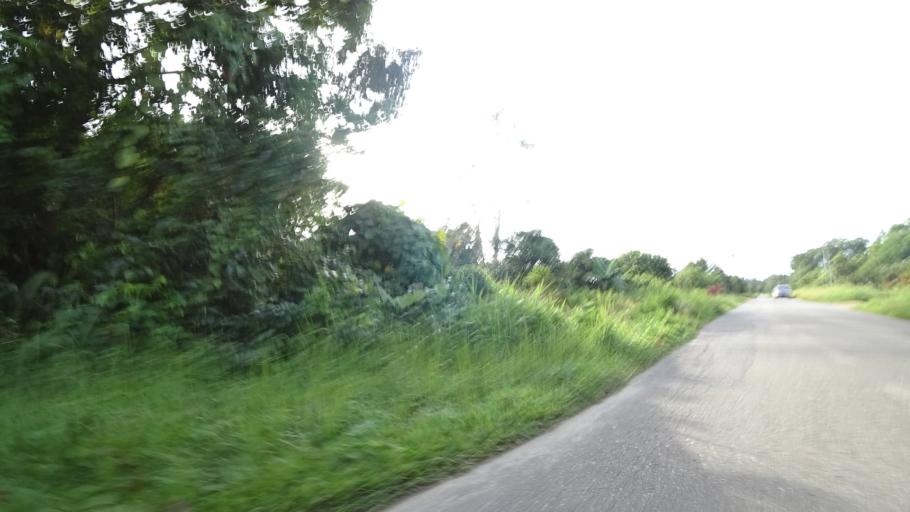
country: BN
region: Brunei and Muara
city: Bandar Seri Begawan
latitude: 4.8144
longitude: 114.8277
